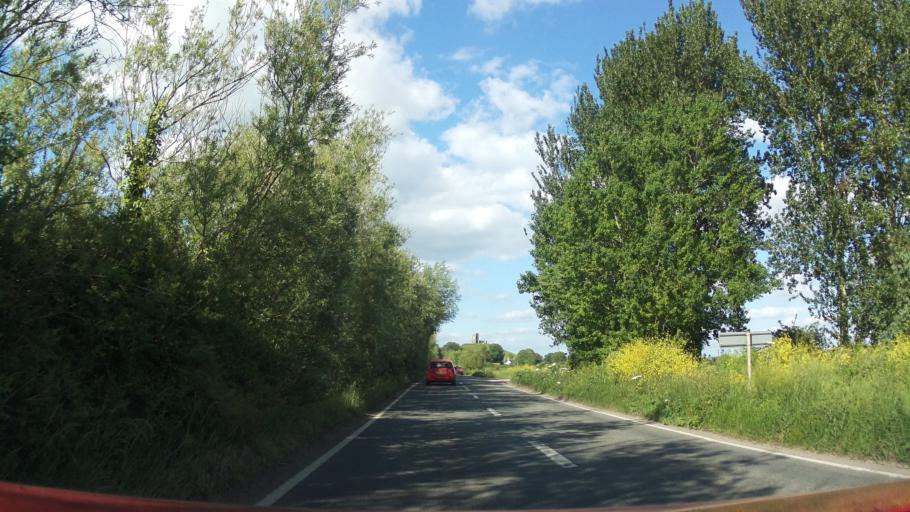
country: GB
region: England
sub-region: Somerset
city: Westonzoyland
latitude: 51.0659
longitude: -2.9249
